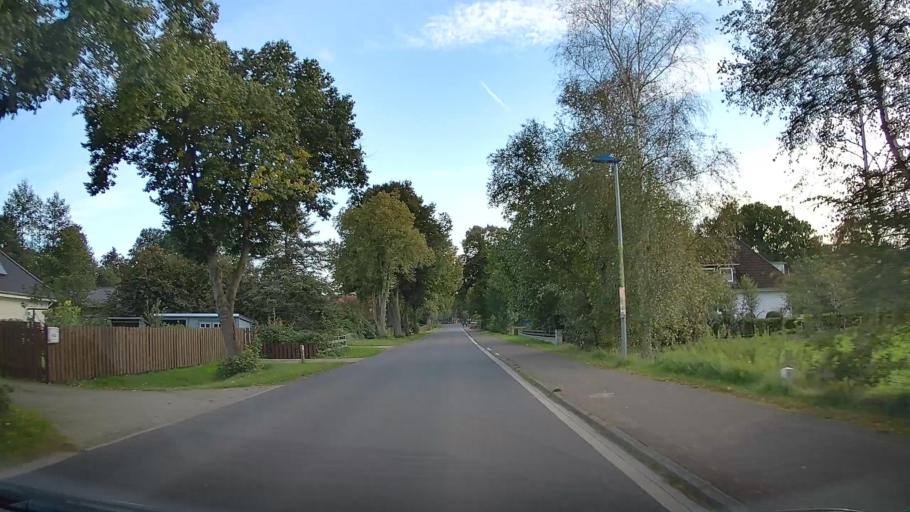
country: DE
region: Lower Saxony
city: Hassendorf
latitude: 53.1087
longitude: 9.2664
